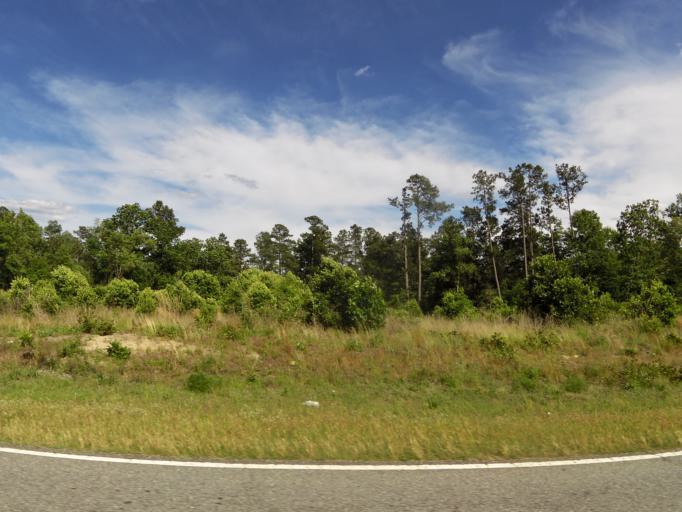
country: US
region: South Carolina
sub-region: Bamberg County
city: Denmark
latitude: 33.2053
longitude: -81.1759
